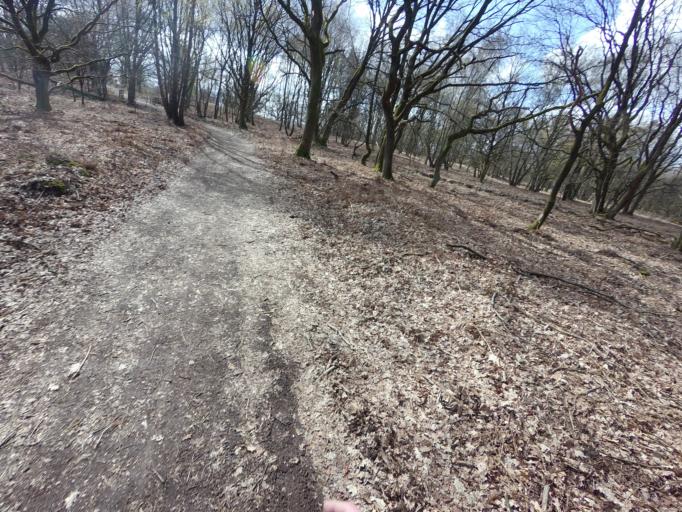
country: NL
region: Limburg
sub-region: Gemeente Roerdalen
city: Vlodrop
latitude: 51.1787
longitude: 6.1286
